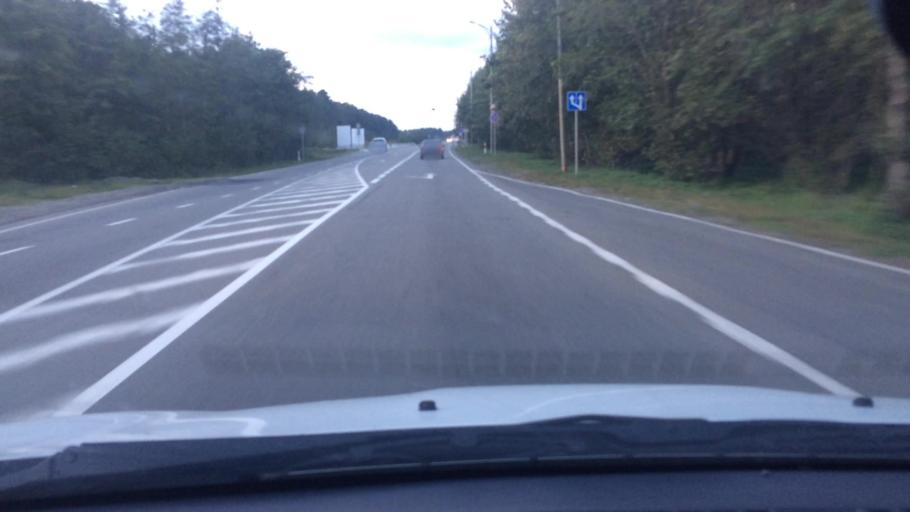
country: GE
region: Guria
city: Urek'i
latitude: 41.9419
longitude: 41.7709
